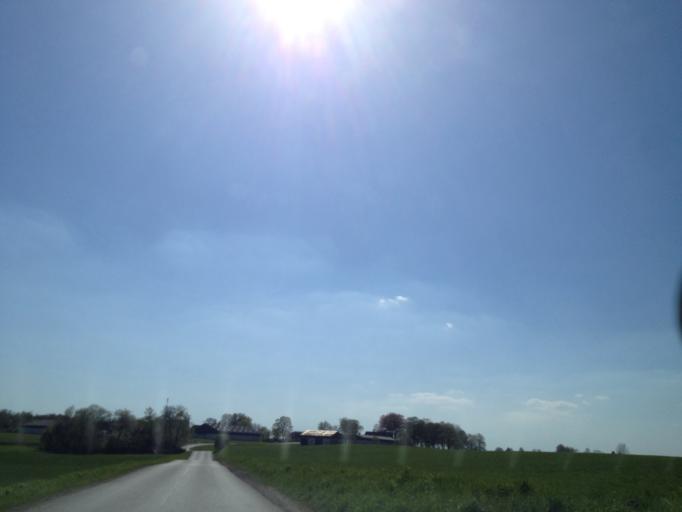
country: DK
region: Zealand
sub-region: Koge Kommune
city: Borup
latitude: 55.4909
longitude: 11.9109
